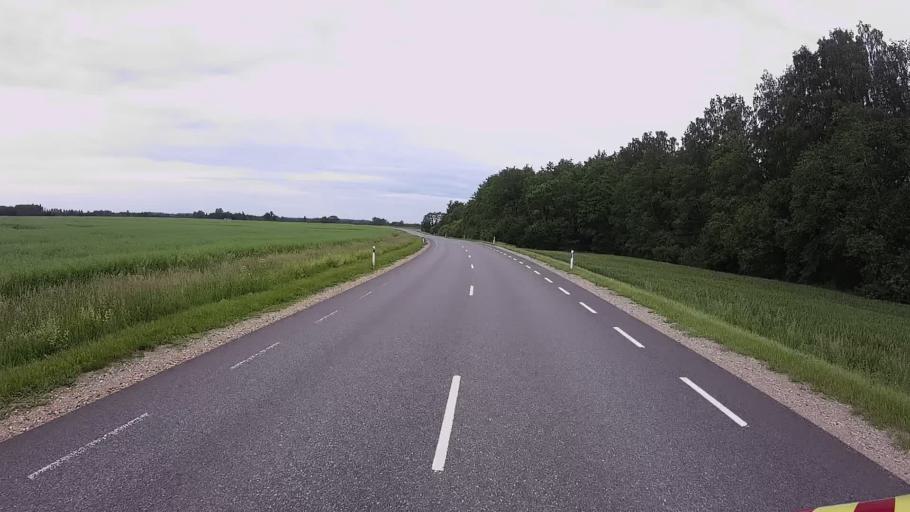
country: EE
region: Viljandimaa
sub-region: Karksi vald
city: Karksi-Nuia
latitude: 58.1747
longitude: 25.5836
